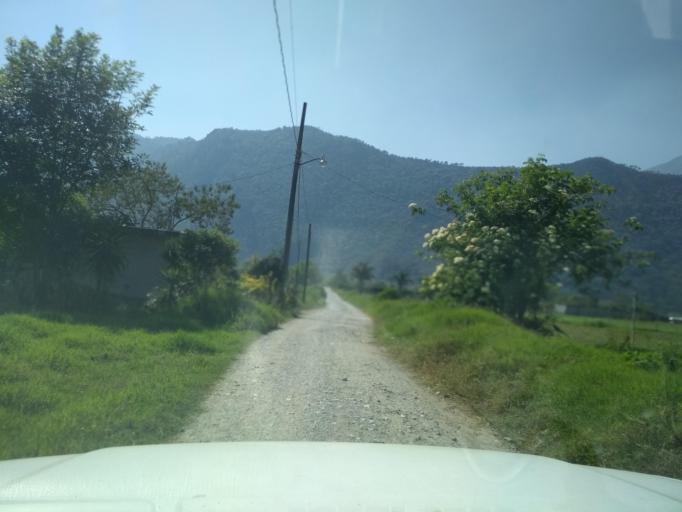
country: MX
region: Veracruz
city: Jalapilla
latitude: 18.8146
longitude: -97.0867
